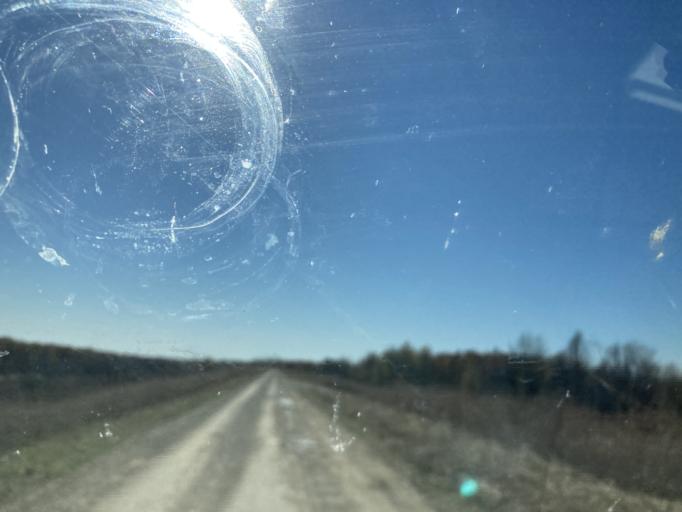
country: US
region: Mississippi
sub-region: Sharkey County
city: Rolling Fork
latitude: 32.7498
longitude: -90.6613
